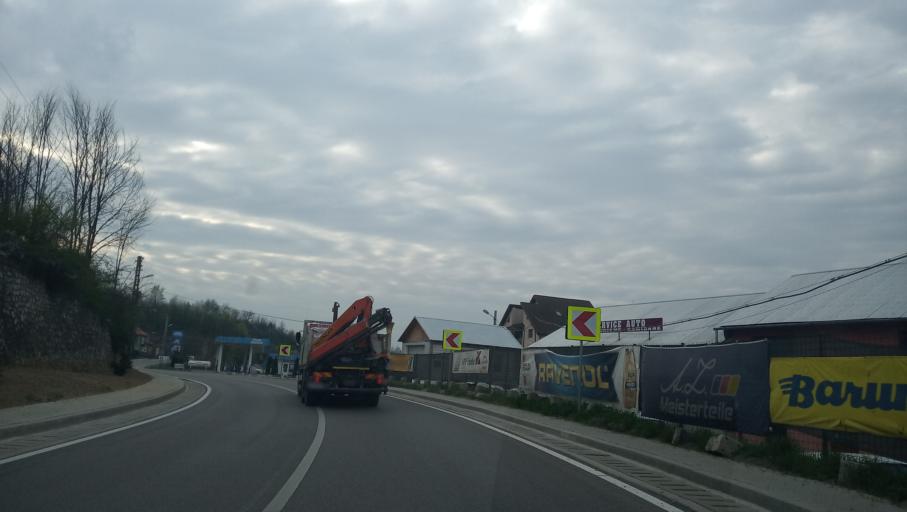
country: RO
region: Bihor
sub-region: Comuna Lunca
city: Lunca
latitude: 46.5285
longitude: 22.4587
